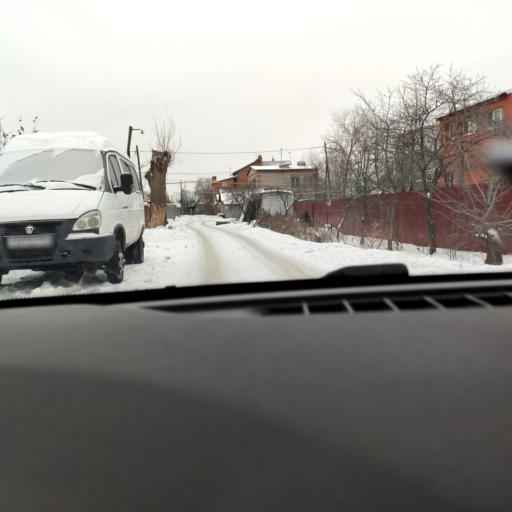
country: RU
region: Samara
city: Smyshlyayevka
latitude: 53.2320
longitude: 50.3027
